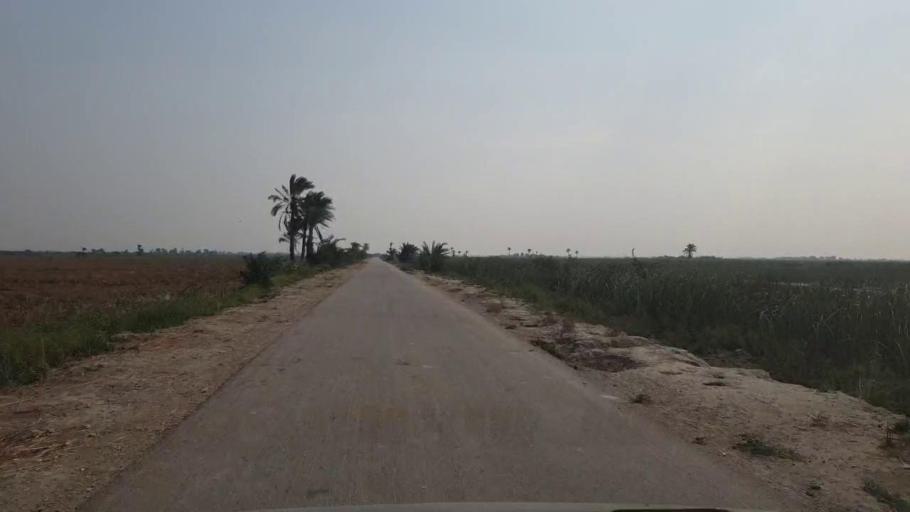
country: PK
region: Sindh
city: Tando Muhammad Khan
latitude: 25.1006
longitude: 68.3748
